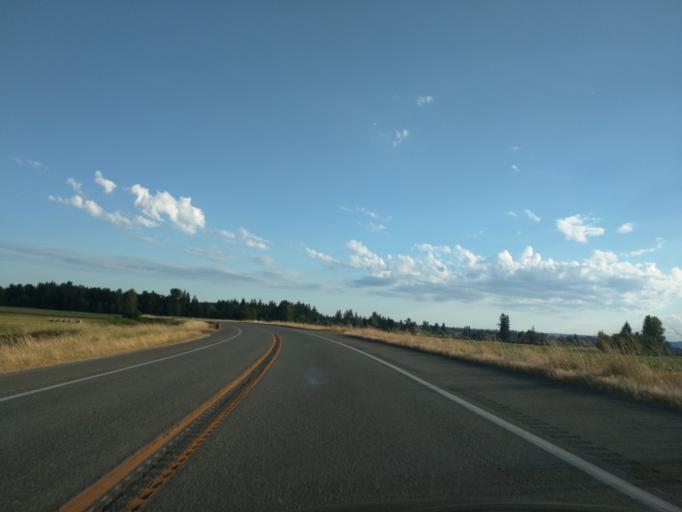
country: US
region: Washington
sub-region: Snohomish County
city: Arlington
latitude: 48.1959
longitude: -122.1384
